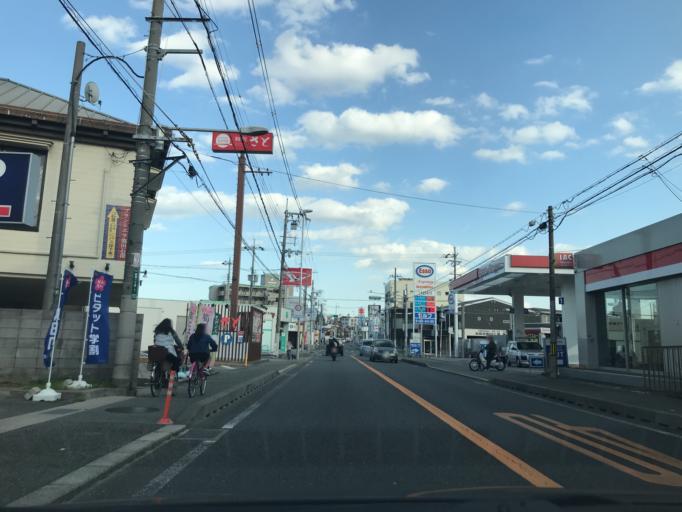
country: JP
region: Osaka
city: Ikeda
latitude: 34.8173
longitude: 135.4345
